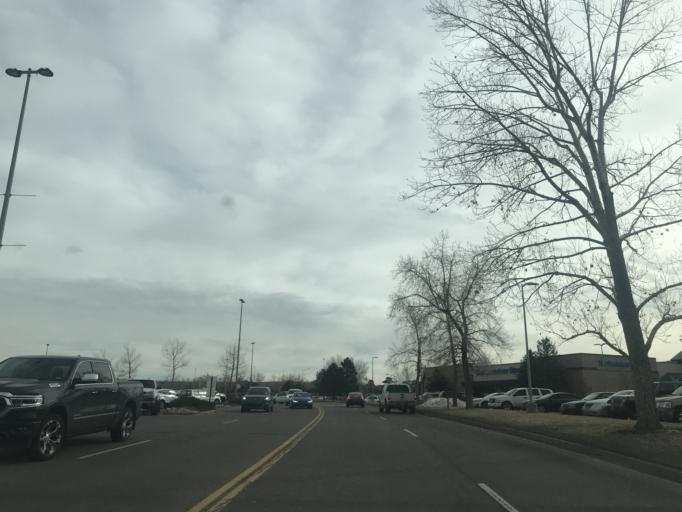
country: US
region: Colorado
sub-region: Adams County
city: Lone Tree
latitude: 39.5606
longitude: -104.8784
